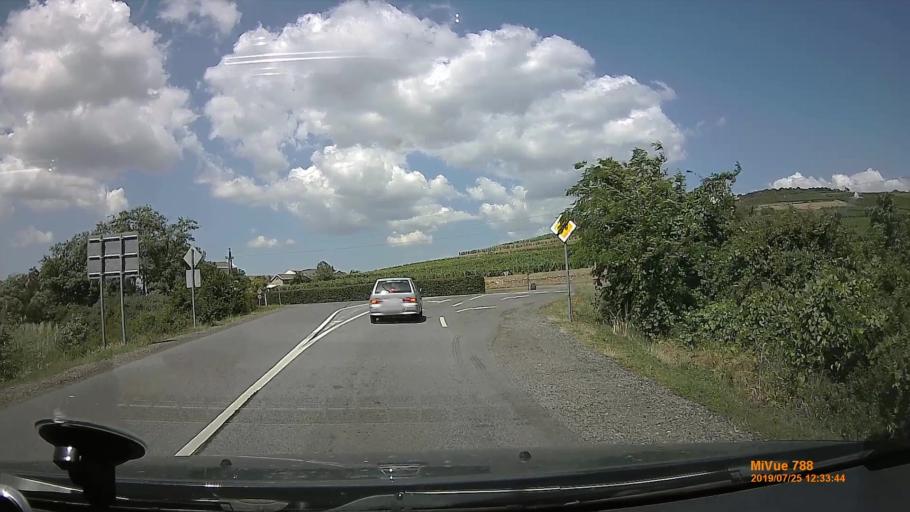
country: HU
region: Borsod-Abauj-Zemplen
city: Mad
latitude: 48.1644
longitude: 21.3051
